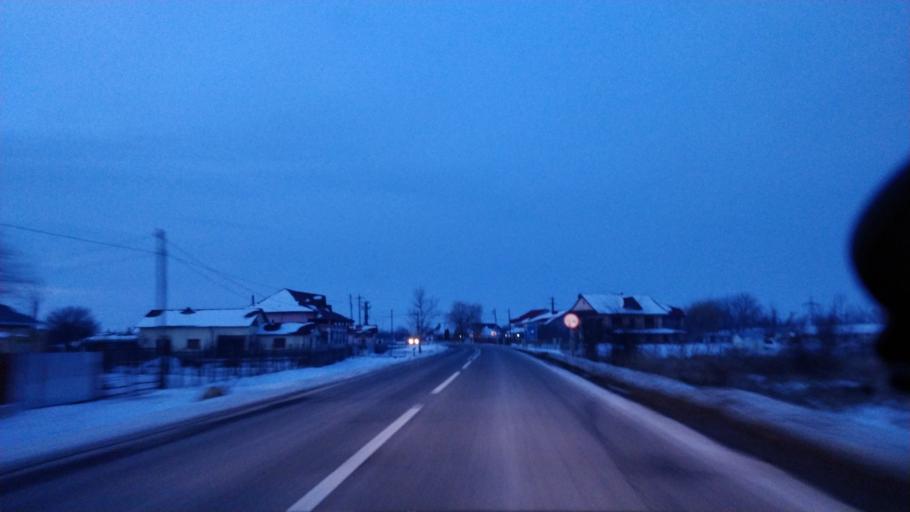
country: RO
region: Vrancea
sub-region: Comuna Nanesti
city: Nanesti
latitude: 45.5852
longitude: 27.4966
